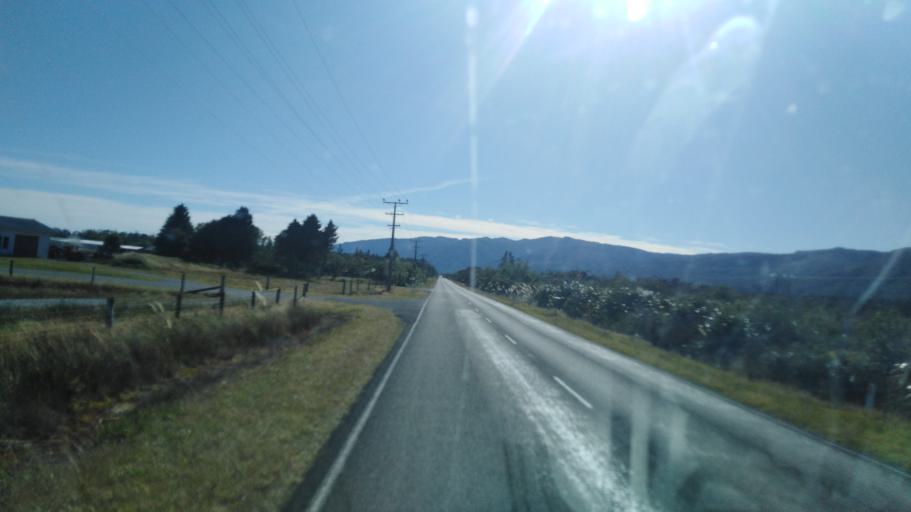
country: NZ
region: West Coast
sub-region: Buller District
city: Westport
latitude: -41.7477
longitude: 171.6801
